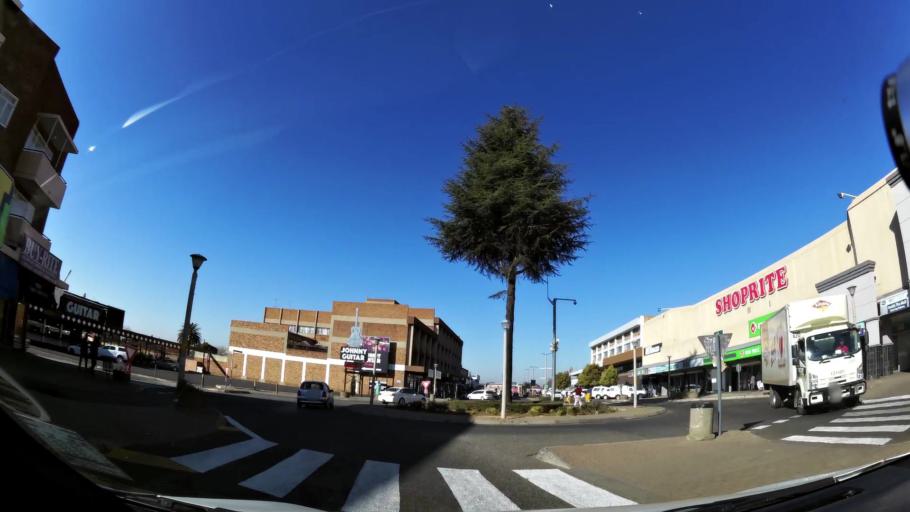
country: ZA
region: Gauteng
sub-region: Ekurhuleni Metropolitan Municipality
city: Germiston
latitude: -26.2692
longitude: 28.1221
